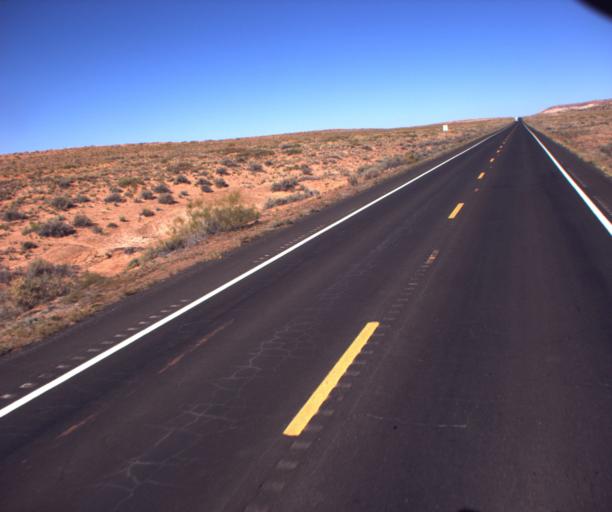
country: US
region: Arizona
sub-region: Coconino County
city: Tuba City
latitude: 36.2112
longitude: -111.0491
